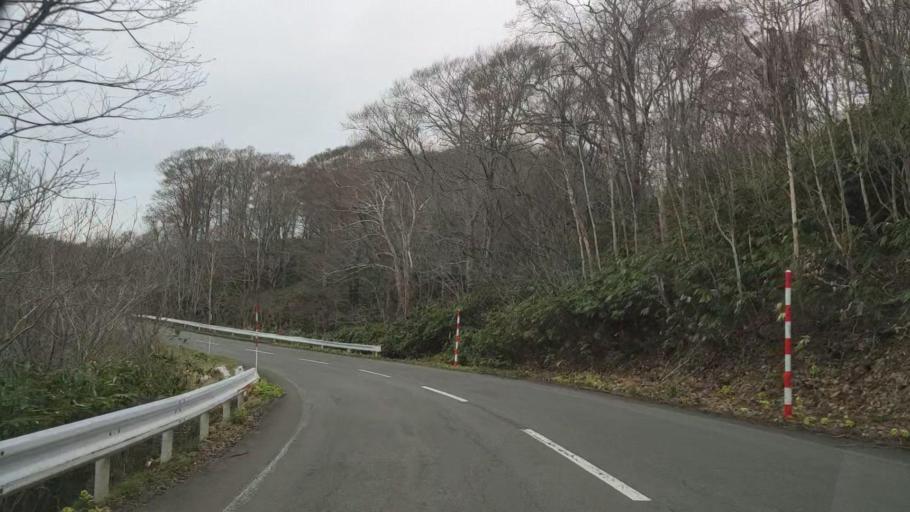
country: JP
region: Akita
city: Hanawa
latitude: 40.4190
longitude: 140.8378
